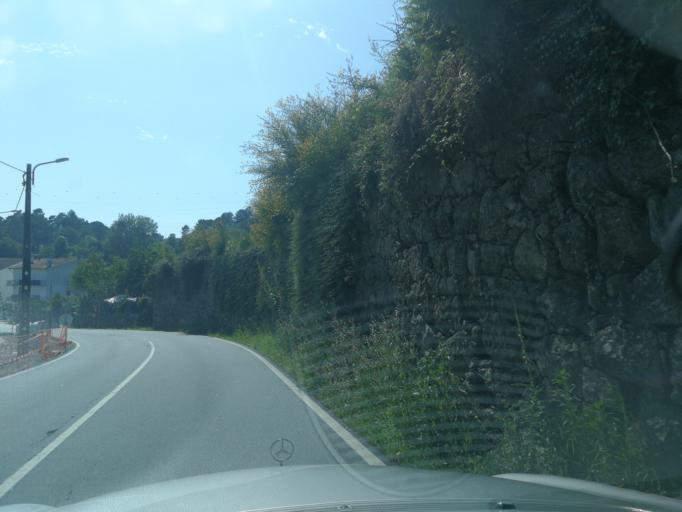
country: PT
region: Braga
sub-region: Braga
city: Adaufe
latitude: 41.5691
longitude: -8.3907
